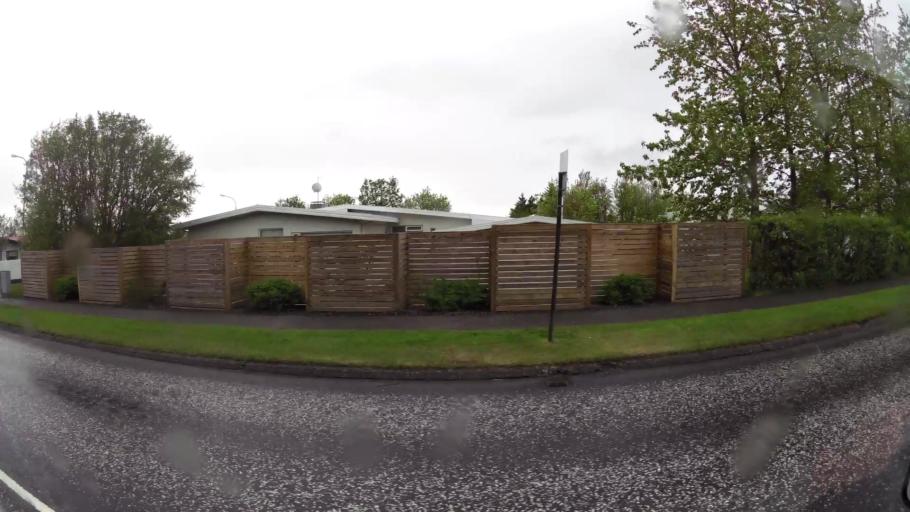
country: IS
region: Capital Region
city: Gardabaer
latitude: 64.0872
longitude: -21.9084
